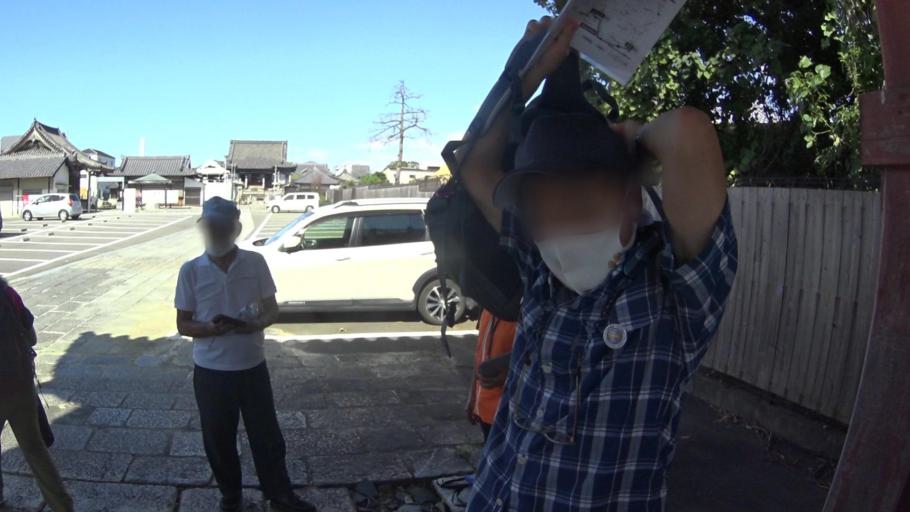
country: JP
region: Ehime
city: Kihoku-cho
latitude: 33.3803
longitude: 132.8204
